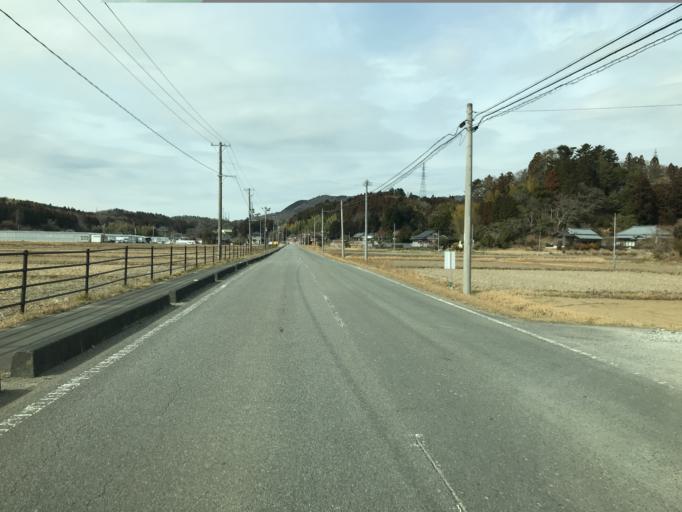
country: JP
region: Fukushima
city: Iwaki
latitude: 37.1183
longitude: 140.9450
